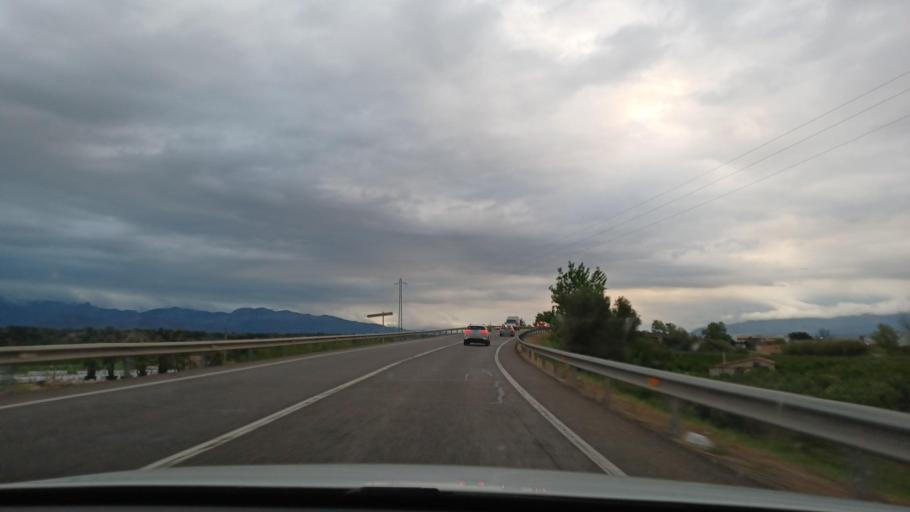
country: ES
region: Catalonia
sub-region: Provincia de Tarragona
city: Tortosa
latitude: 40.7892
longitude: 0.4965
